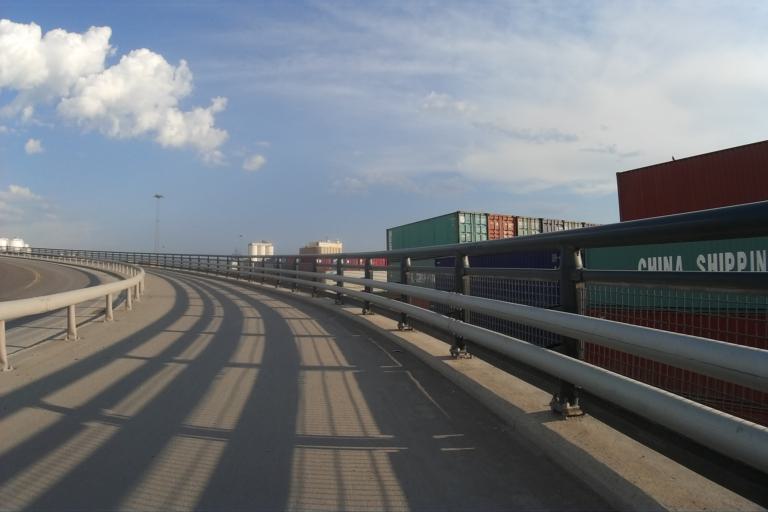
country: NO
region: Oslo
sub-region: Oslo
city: Oslo
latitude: 59.8949
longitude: 10.7555
